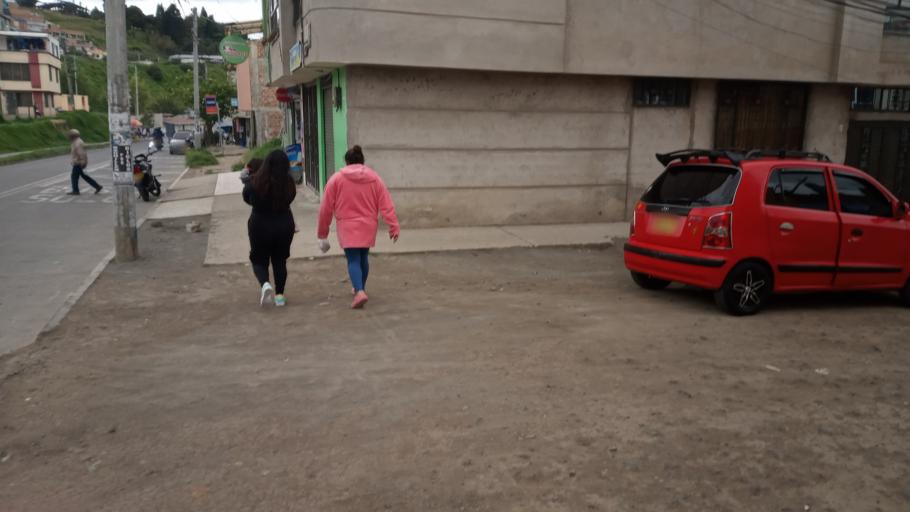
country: CO
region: Narino
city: Pasto
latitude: 1.1978
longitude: -77.2849
